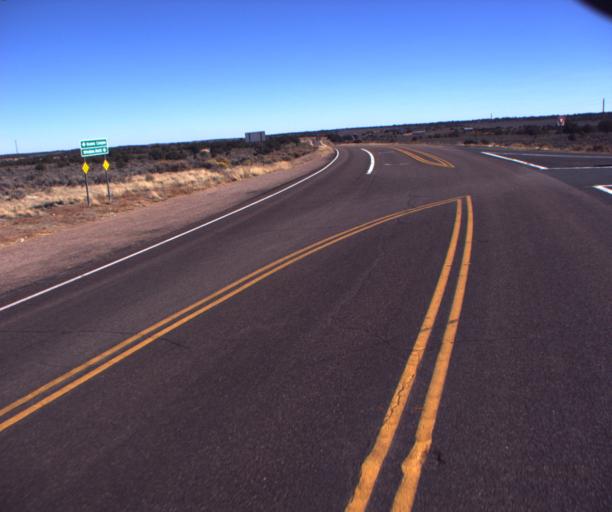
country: US
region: Arizona
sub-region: Navajo County
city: First Mesa
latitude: 35.7333
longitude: -110.1082
